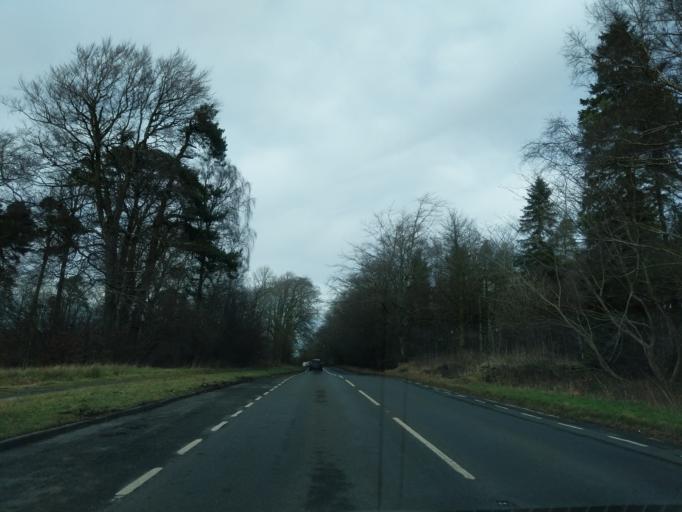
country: GB
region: Scotland
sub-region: Midlothian
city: Penicuik
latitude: 55.8173
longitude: -3.2023
